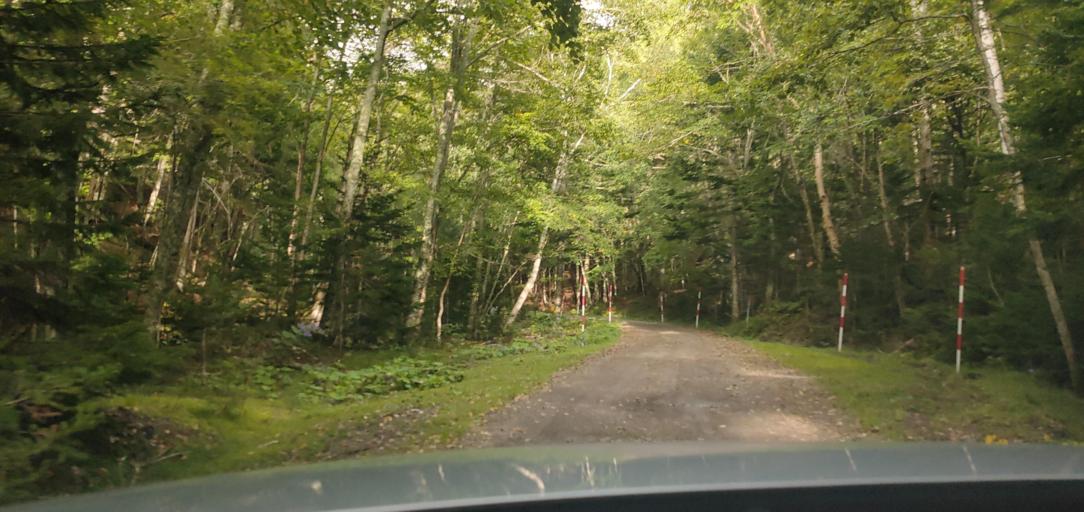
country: JP
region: Hokkaido
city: Kitami
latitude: 43.3721
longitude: 143.9575
